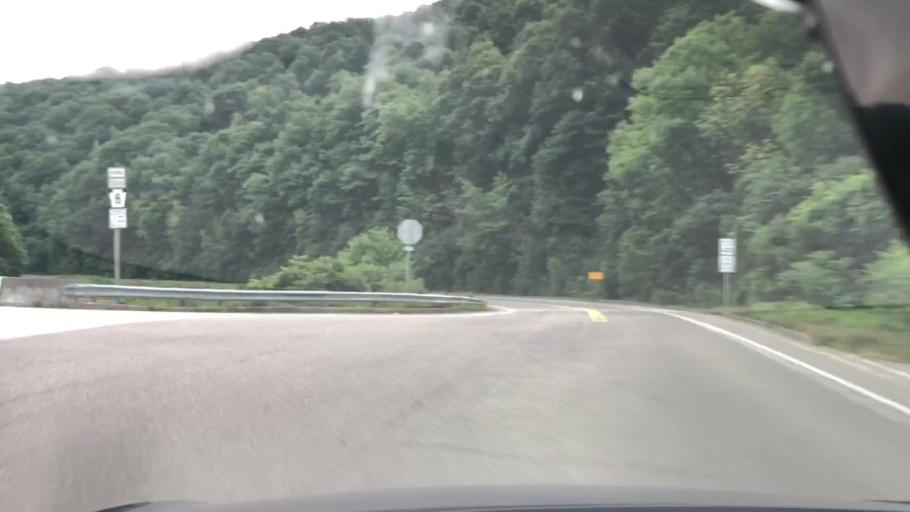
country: US
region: Pennsylvania
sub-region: Venango County
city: Oil City
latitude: 41.4432
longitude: -79.7061
